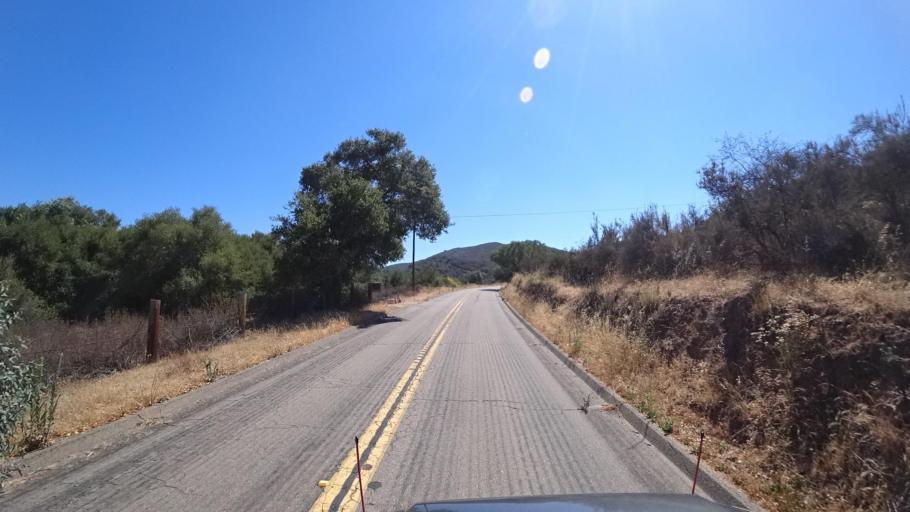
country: US
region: California
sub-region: San Diego County
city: Rainbow
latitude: 33.3391
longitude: -117.0811
